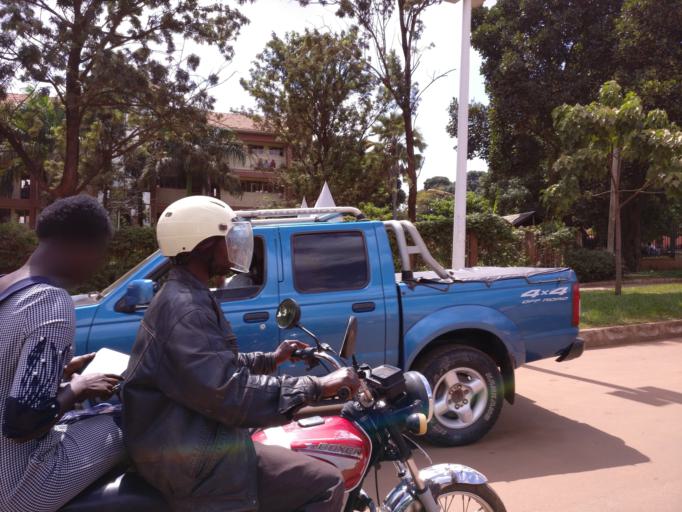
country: UG
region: Central Region
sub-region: Kampala District
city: Kampala
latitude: 0.3051
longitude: 32.5631
